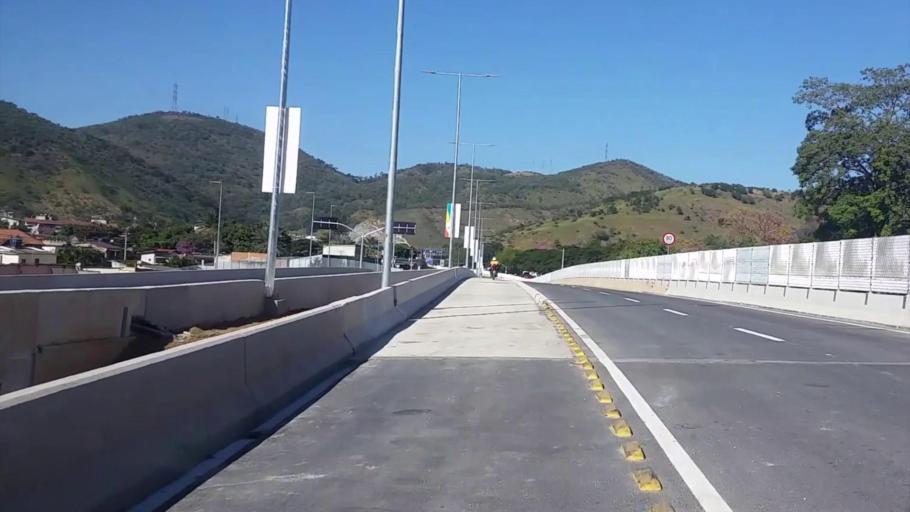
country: BR
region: Rio de Janeiro
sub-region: Nilopolis
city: Nilopolis
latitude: -22.8852
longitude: -43.4007
